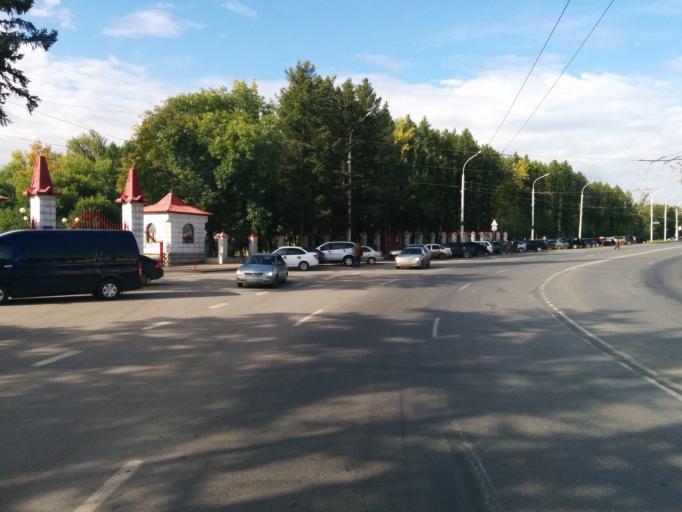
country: RU
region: Bashkortostan
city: Ufa
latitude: 54.8198
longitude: 56.0570
